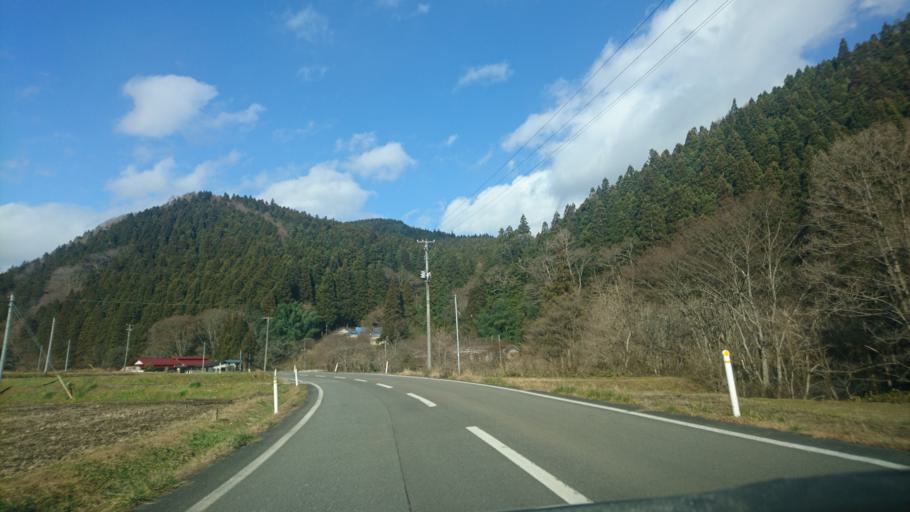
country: JP
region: Iwate
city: Mizusawa
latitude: 39.0832
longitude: 141.3910
